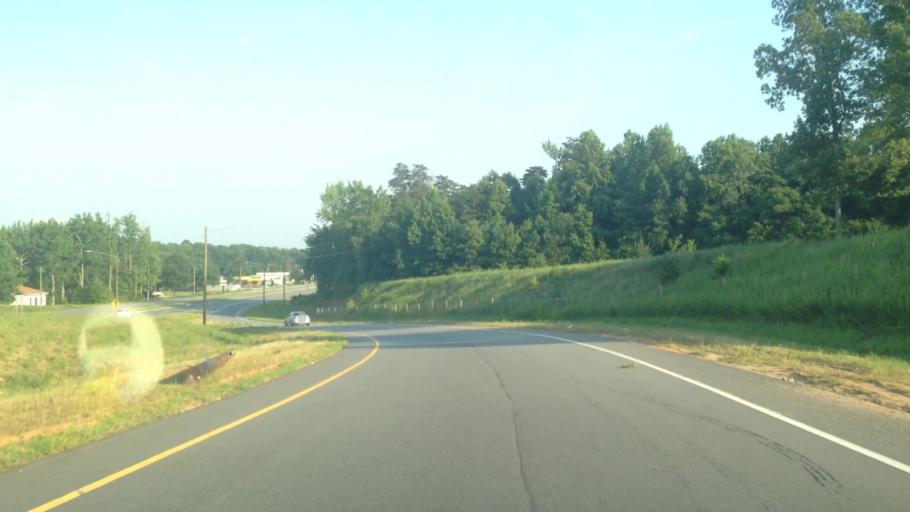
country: US
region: North Carolina
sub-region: Rockingham County
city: Reidsville
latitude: 36.3336
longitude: -79.6932
